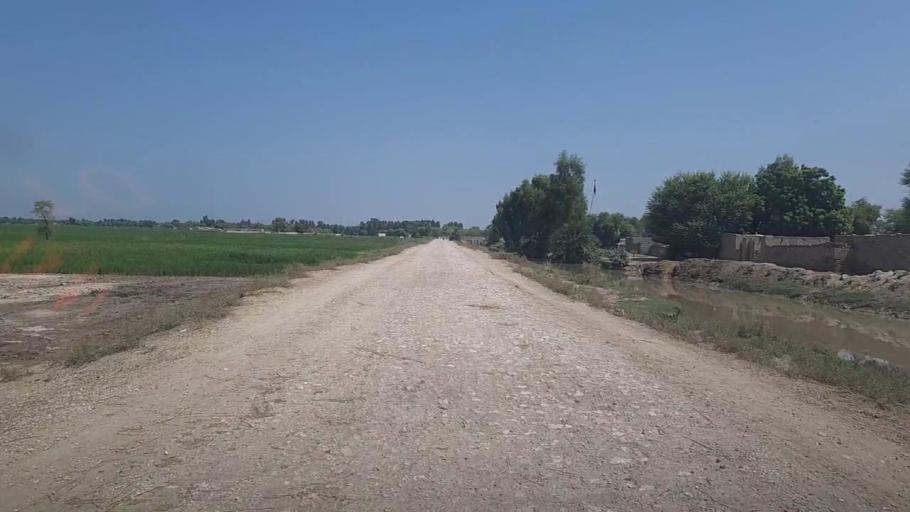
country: PK
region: Sindh
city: Kandhkot
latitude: 28.2706
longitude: 69.2225
